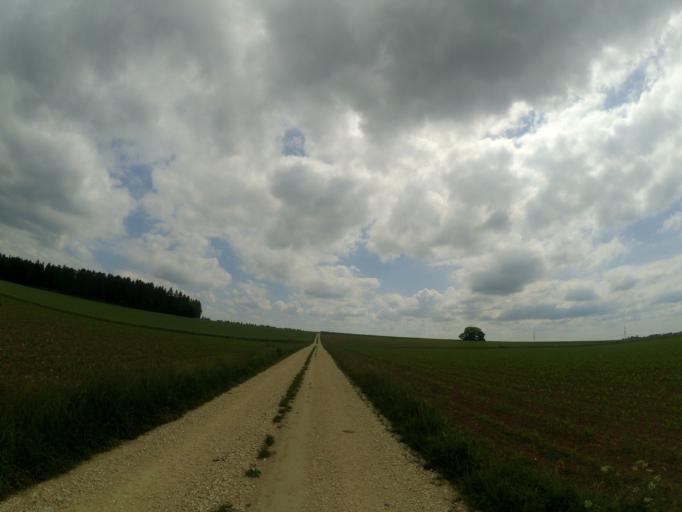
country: DE
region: Baden-Wuerttemberg
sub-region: Tuebingen Region
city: Blaubeuren
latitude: 48.4243
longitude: 9.8296
